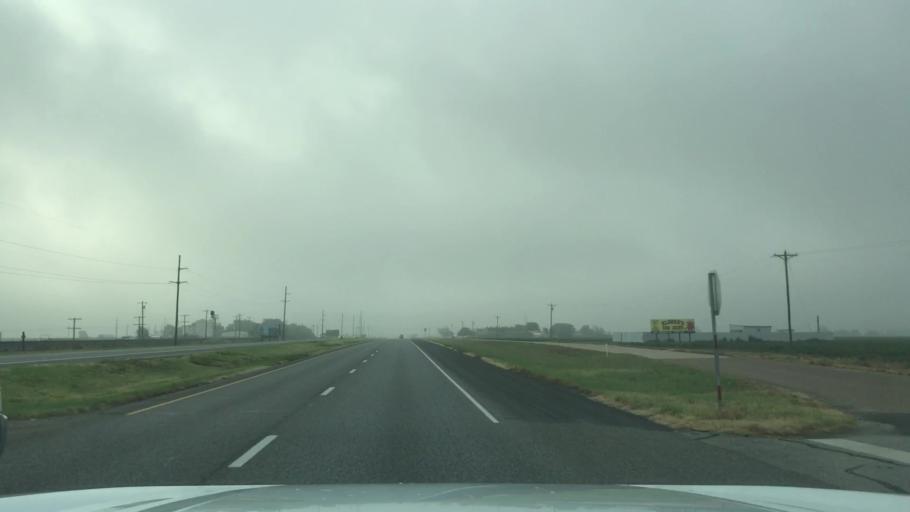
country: US
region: Texas
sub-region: Lubbock County
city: Ransom Canyon
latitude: 33.4862
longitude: -101.7173
